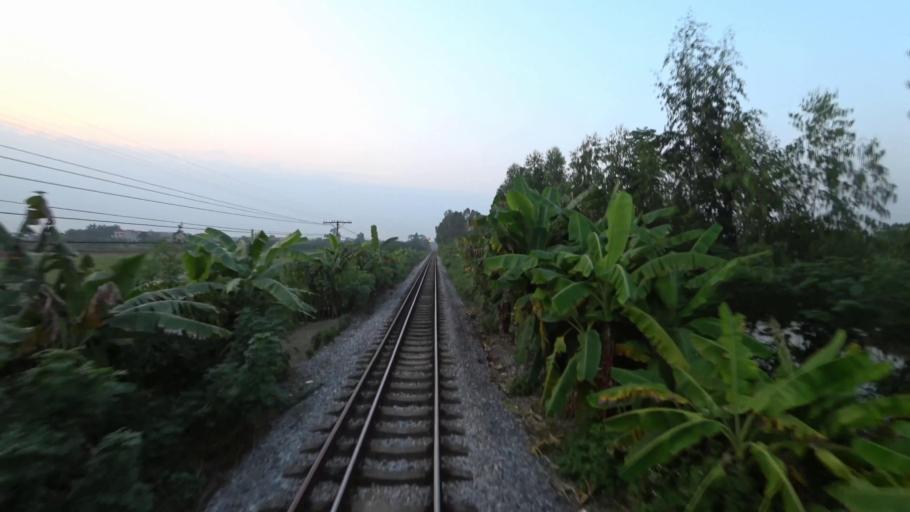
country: VN
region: Ha Noi
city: Dong Anh
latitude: 21.1495
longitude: 105.8568
